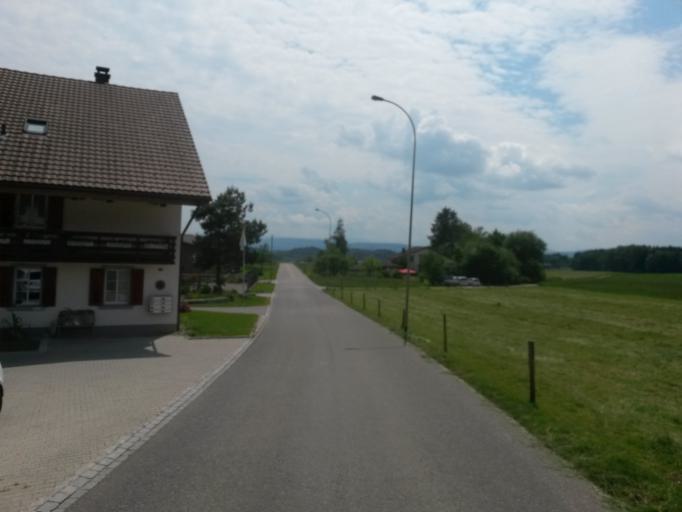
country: CH
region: Zurich
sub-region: Bezirk Winterthur
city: Brutten
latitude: 47.4563
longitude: 8.6855
